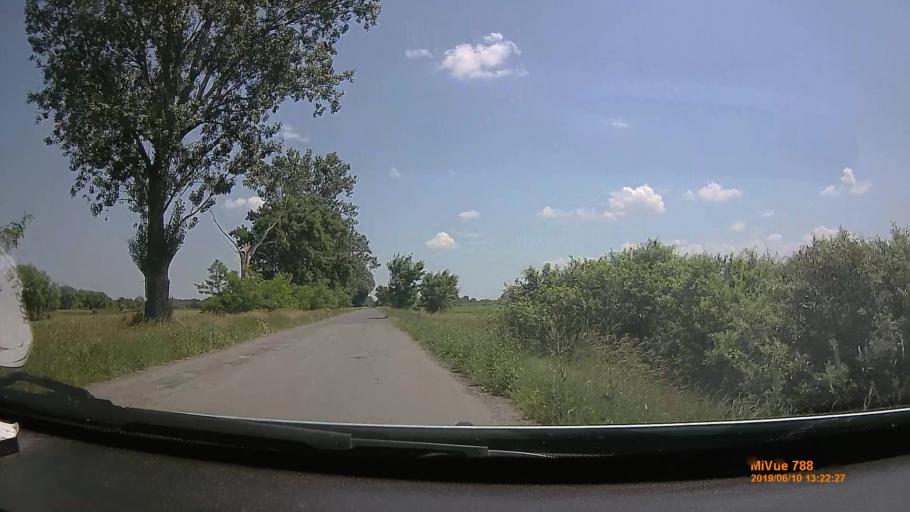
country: HU
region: Borsod-Abauj-Zemplen
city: Tiszaluc
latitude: 48.0298
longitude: 21.0828
